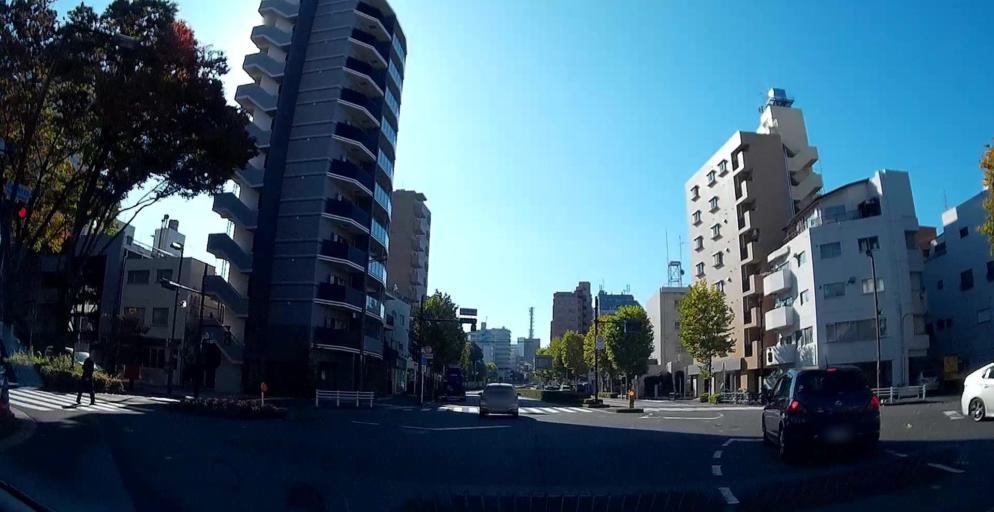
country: JP
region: Tokyo
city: Tokyo
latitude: 35.7075
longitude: 139.7270
